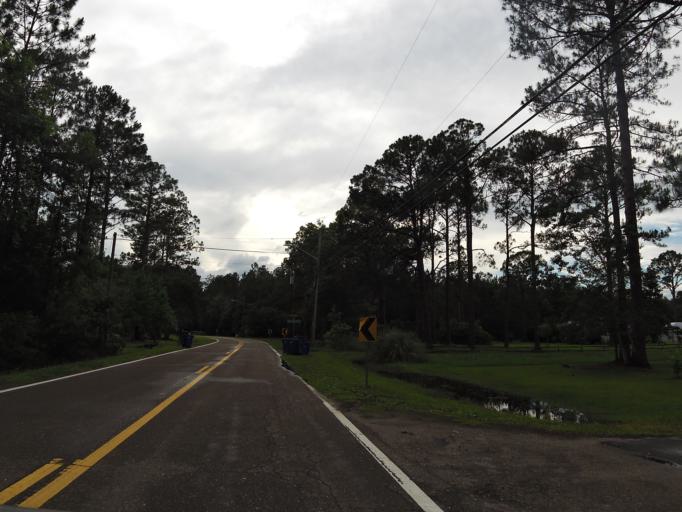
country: US
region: Florida
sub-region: Nassau County
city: Nassau Village-Ratliff
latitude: 30.5511
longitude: -81.7041
